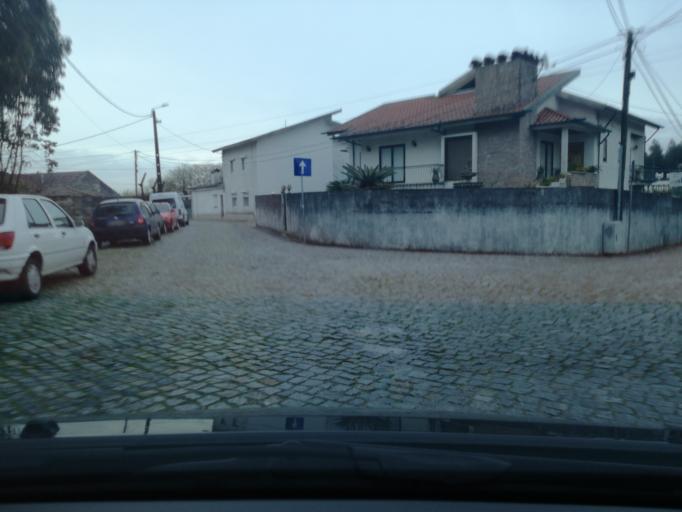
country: PT
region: Porto
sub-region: Maia
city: Gemunde
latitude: 41.2628
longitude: -8.6648
